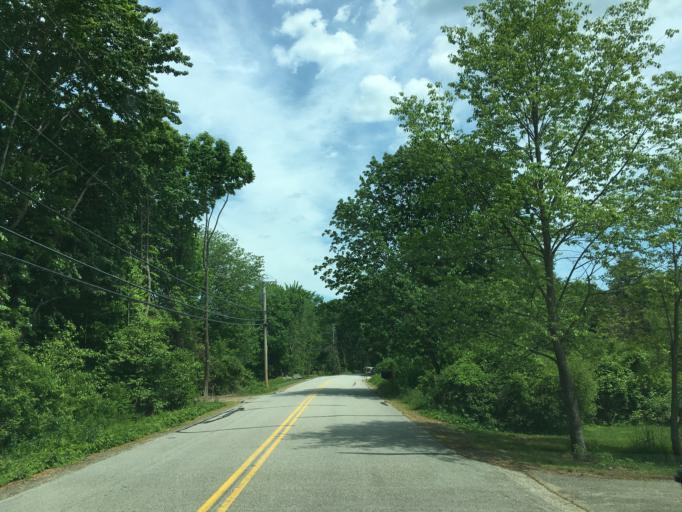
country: US
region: New Hampshire
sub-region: Rockingham County
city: Stratham Station
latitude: 43.0235
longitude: -70.8926
